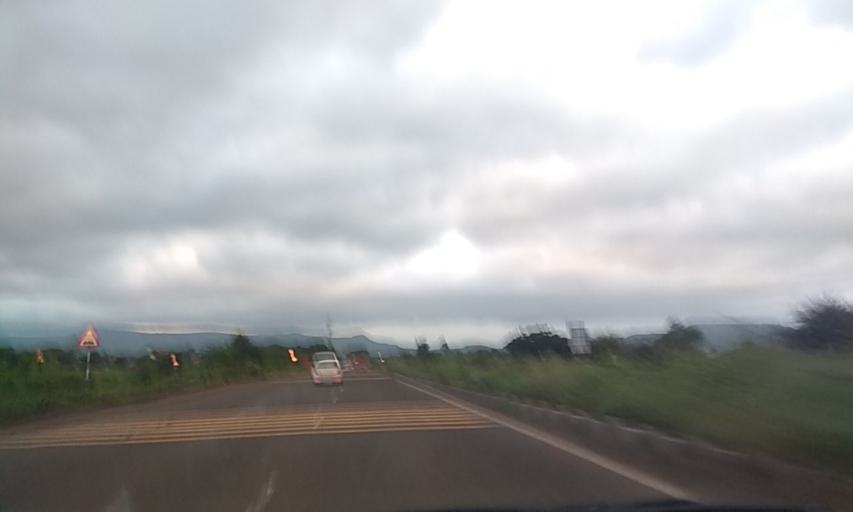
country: IN
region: Maharashtra
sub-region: Satara Division
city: Wai
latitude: 17.9405
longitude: 73.9773
